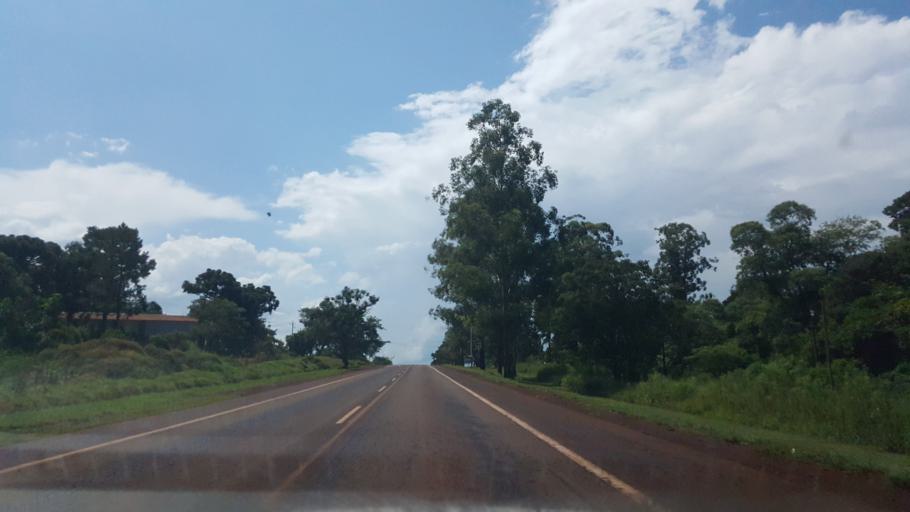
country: AR
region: Misiones
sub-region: Departamento de Eldorado
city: Eldorado
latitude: -26.3893
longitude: -54.6301
